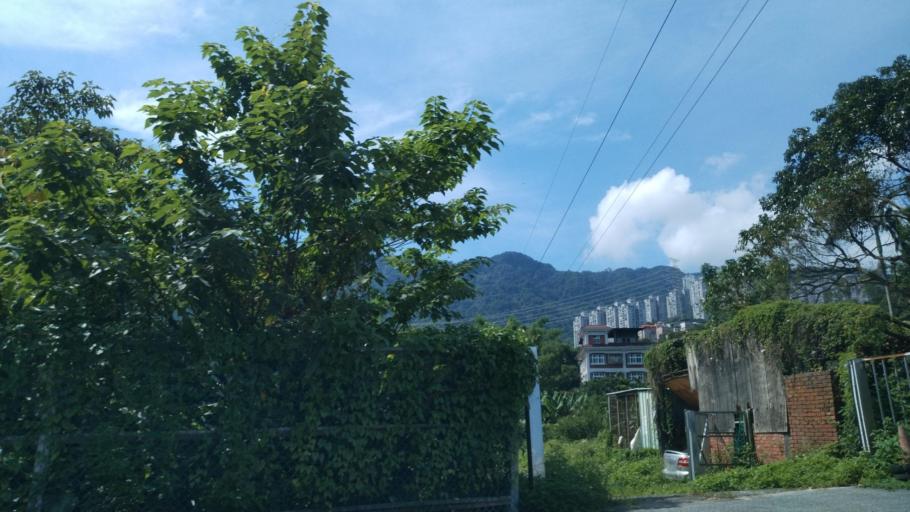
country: TW
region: Taipei
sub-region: Taipei
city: Banqiao
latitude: 24.9524
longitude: 121.5036
